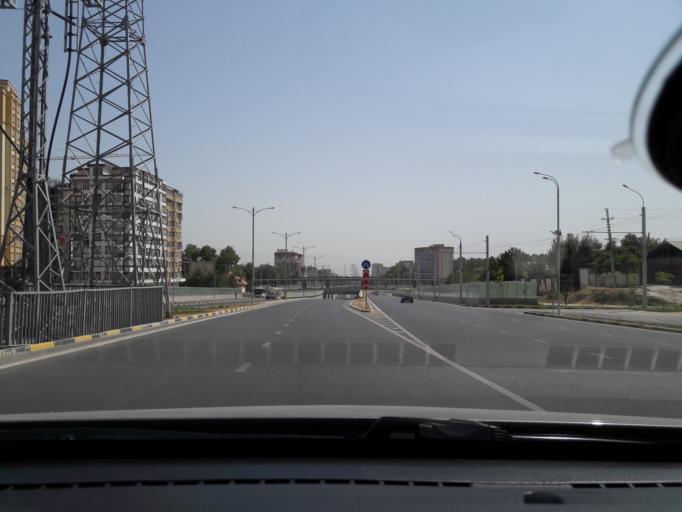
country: TJ
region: Dushanbe
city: Dushanbe
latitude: 38.5865
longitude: 68.7411
